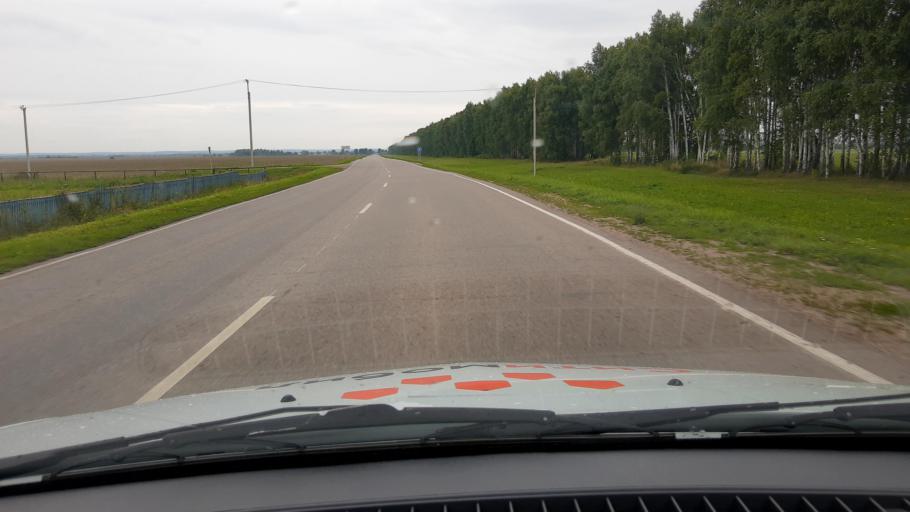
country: RU
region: Bashkortostan
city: Krasnaya Gorka
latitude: 55.0972
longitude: 56.6228
